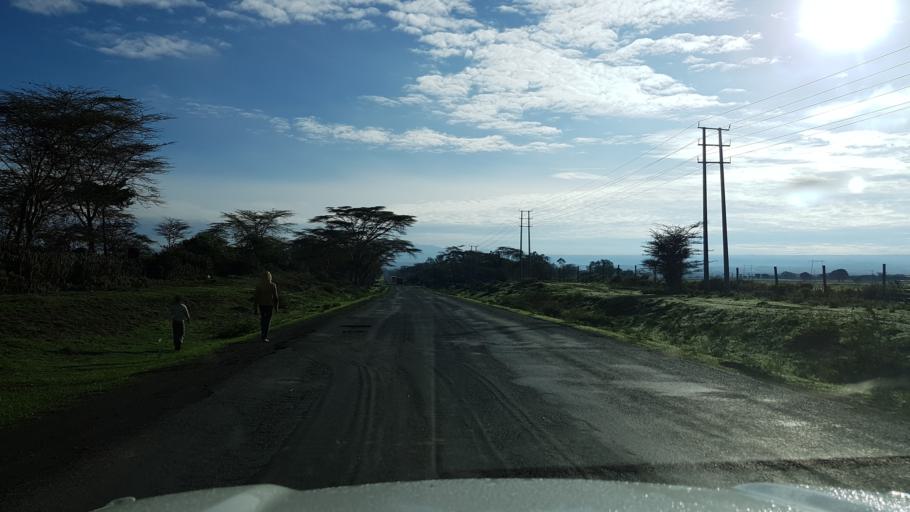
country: KE
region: Nakuru
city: Naivasha
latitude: -0.8160
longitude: 36.3953
